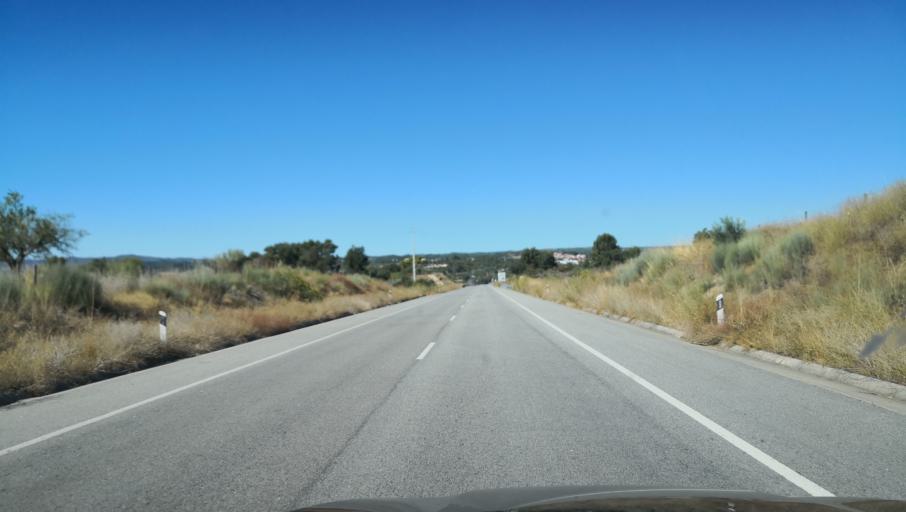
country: PT
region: Vila Real
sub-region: Valpacos
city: Valpacos
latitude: 41.5769
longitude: -7.3026
